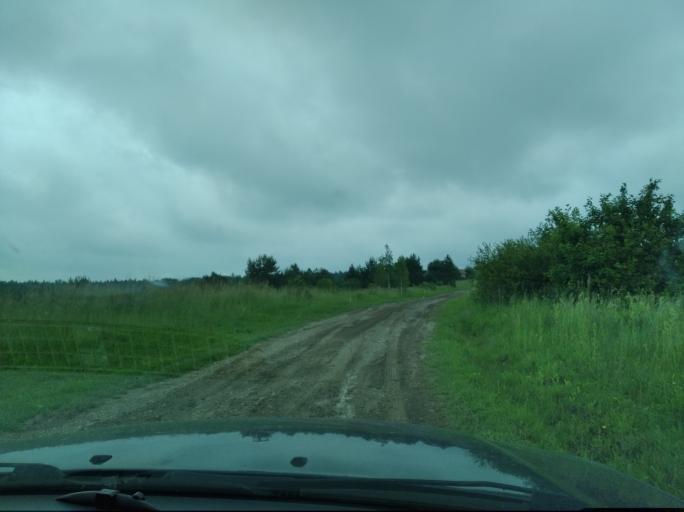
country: PL
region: Subcarpathian Voivodeship
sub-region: Powiat jaroslawski
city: Pruchnik
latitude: 49.8878
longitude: 22.5142
